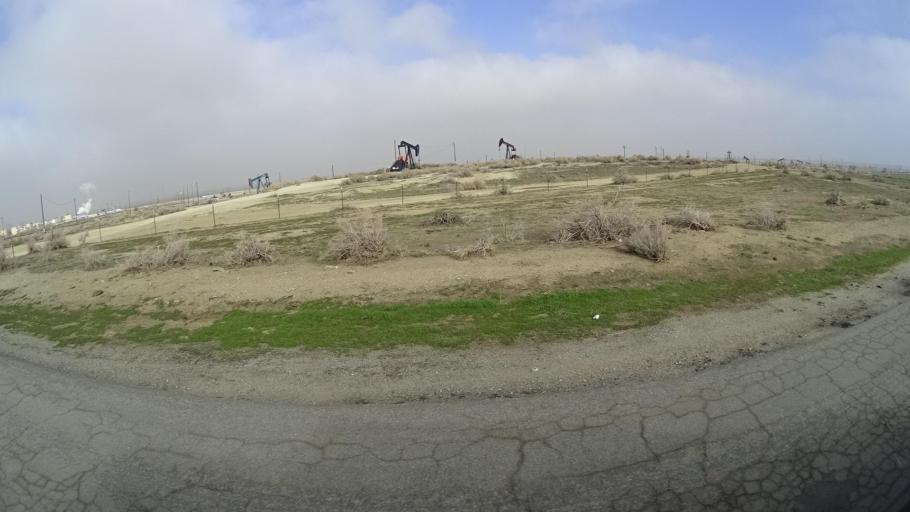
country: US
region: California
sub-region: Kern County
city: Maricopa
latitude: 35.0289
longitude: -119.3415
